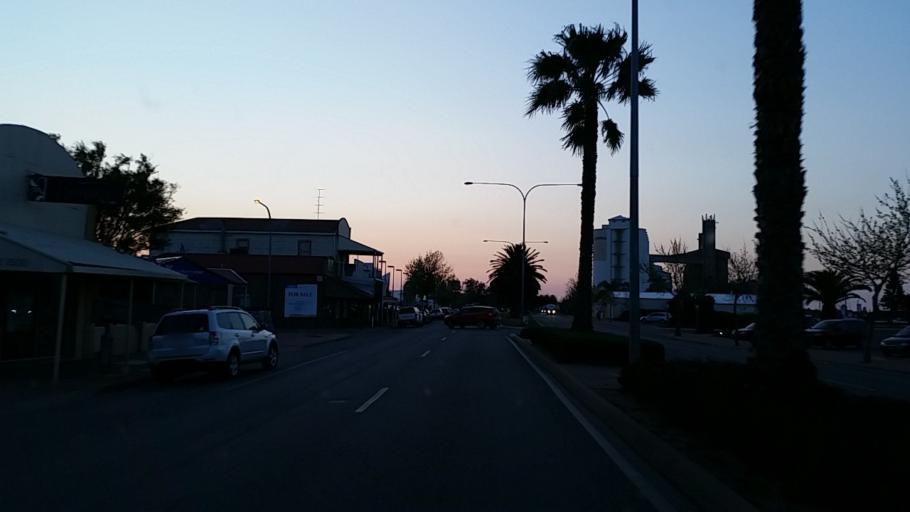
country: AU
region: South Australia
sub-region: Port Pirie City and Dists
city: Port Pirie
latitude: -33.1833
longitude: 138.0177
